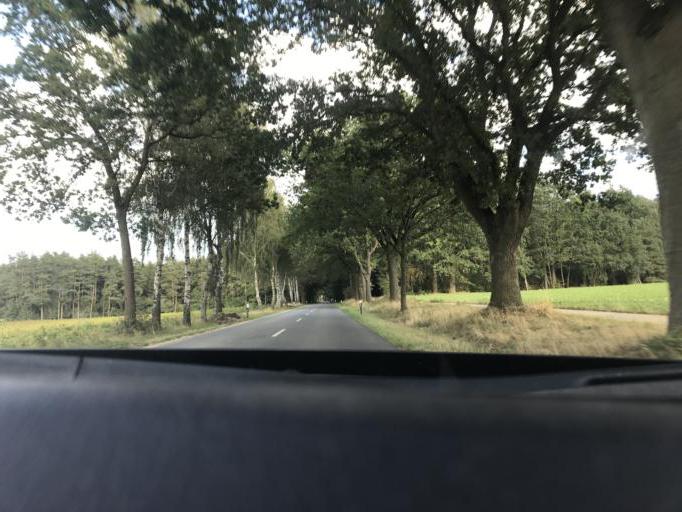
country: DE
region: Lower Saxony
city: Suderburg
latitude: 52.8905
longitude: 10.4818
